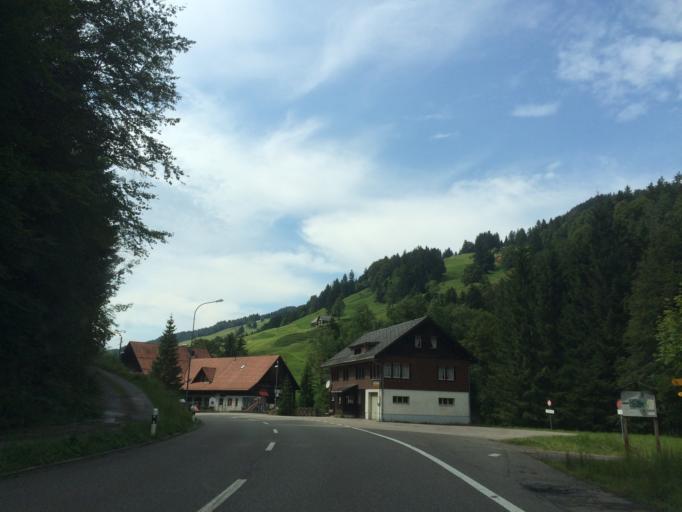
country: CH
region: Appenzell Ausserrhoden
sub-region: Bezirk Hinterland
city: Urnasch
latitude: 47.2457
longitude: 9.2517
